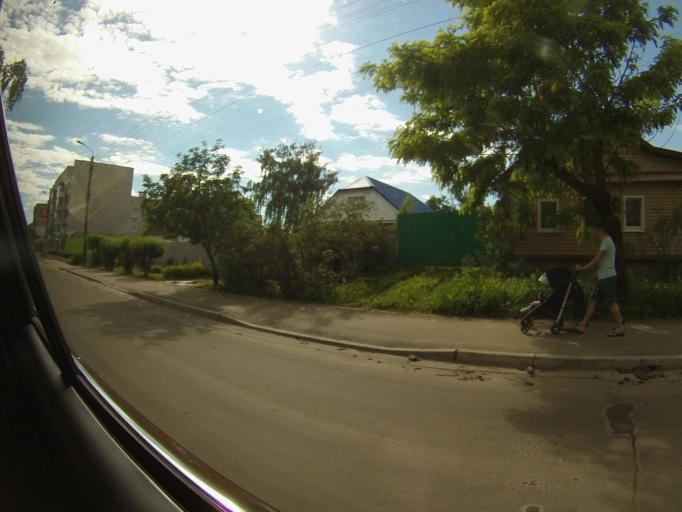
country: RU
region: Orjol
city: Mtsensk
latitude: 53.2839
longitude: 36.5811
